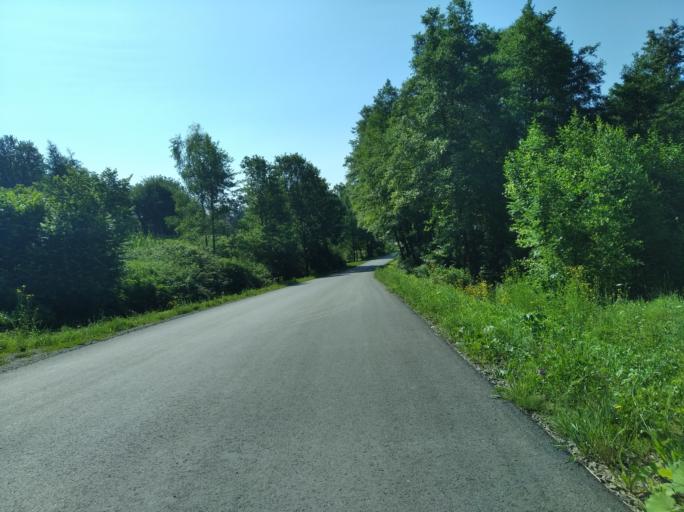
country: PL
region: Subcarpathian Voivodeship
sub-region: Powiat brzozowski
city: Wesola
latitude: 49.8297
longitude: 22.1493
